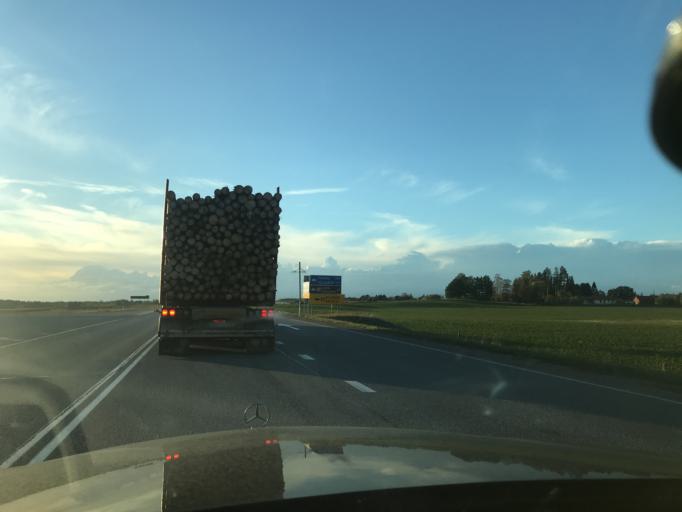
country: EE
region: Vorumaa
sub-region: Voru linn
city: Voru
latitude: 57.8704
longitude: 26.9286
